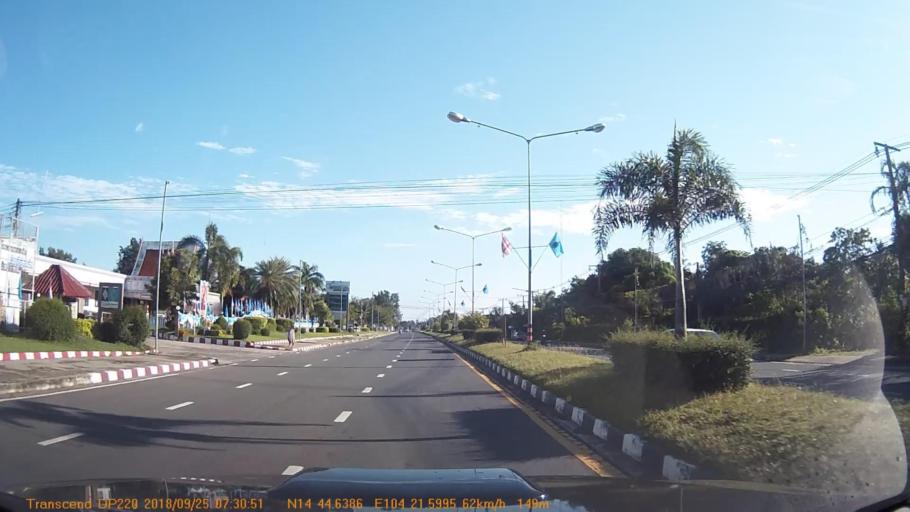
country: TH
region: Sisaket
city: Phrai Bueng
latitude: 14.7442
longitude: 104.3601
